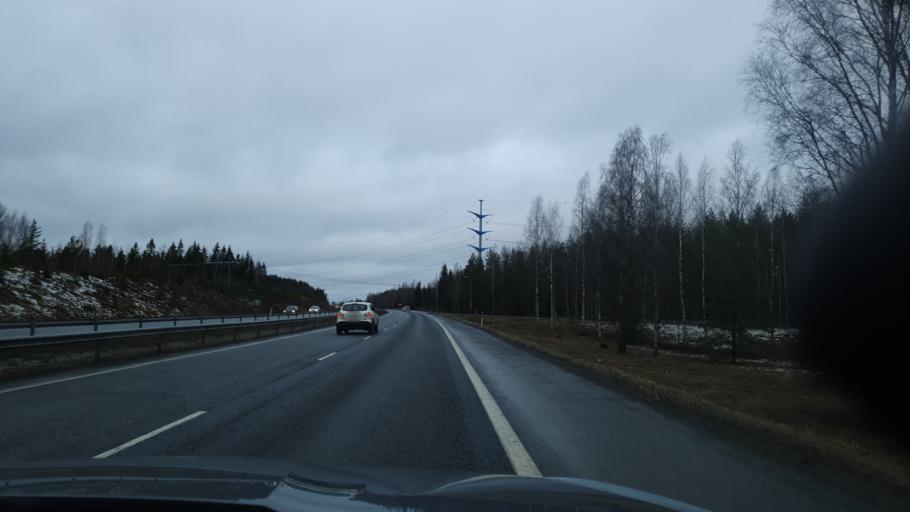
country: FI
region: Pirkanmaa
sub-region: Tampere
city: Lempaeaelae
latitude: 61.3987
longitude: 23.7809
